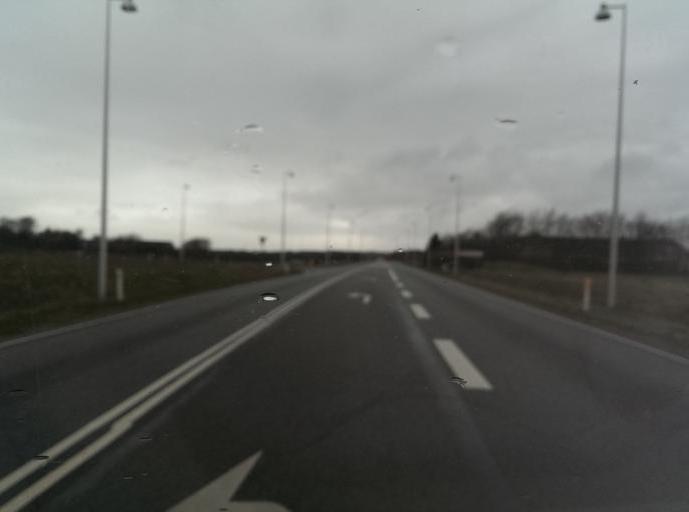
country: DK
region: South Denmark
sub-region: Esbjerg Kommune
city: Tjaereborg
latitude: 55.4945
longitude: 8.6237
